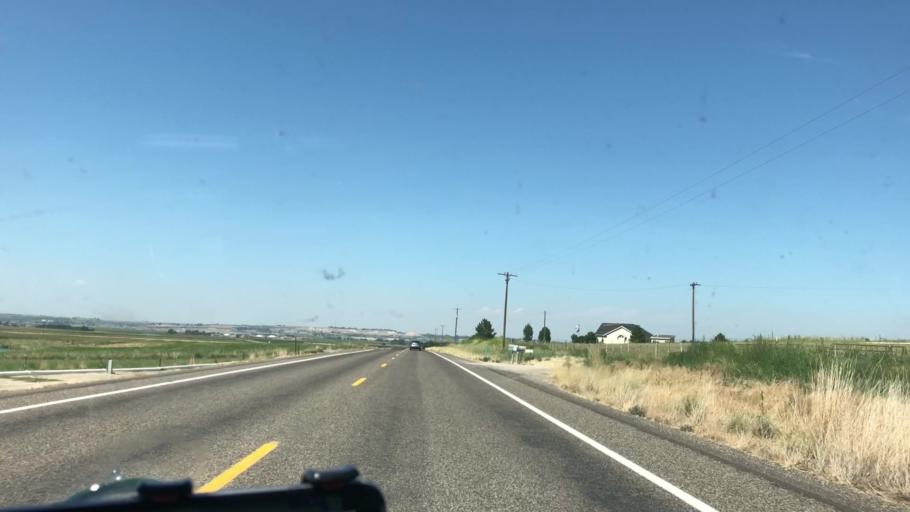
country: US
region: Idaho
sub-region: Owyhee County
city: Marsing
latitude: 43.5173
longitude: -116.8531
